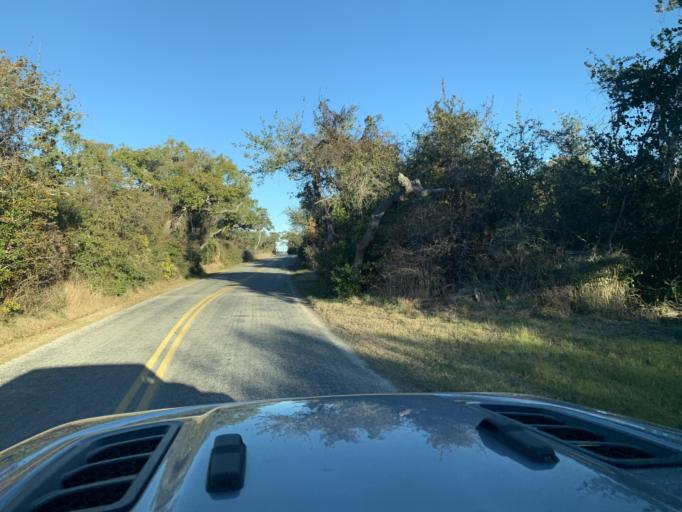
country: US
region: Texas
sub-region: Aransas County
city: Fulton
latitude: 28.1518
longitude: -96.9806
